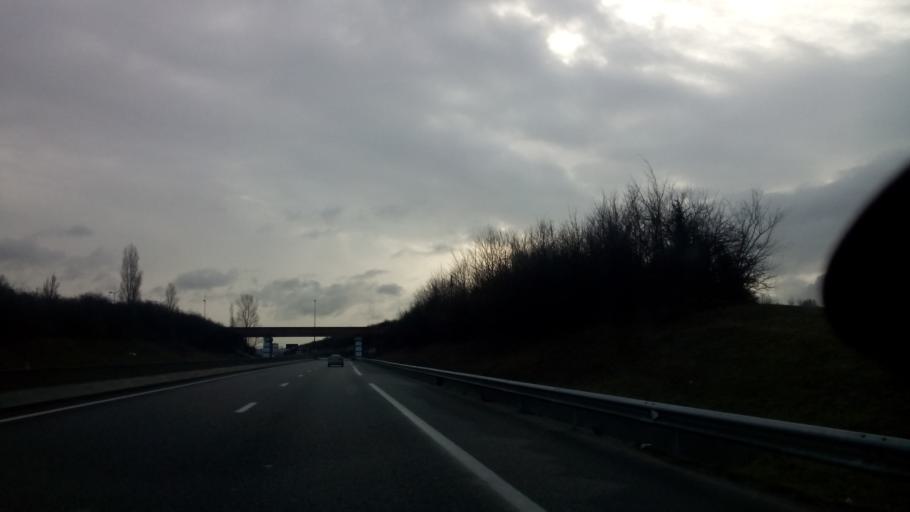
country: FR
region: Rhone-Alpes
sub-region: Departement du Rhone
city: Corbas
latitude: 45.6783
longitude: 4.8984
